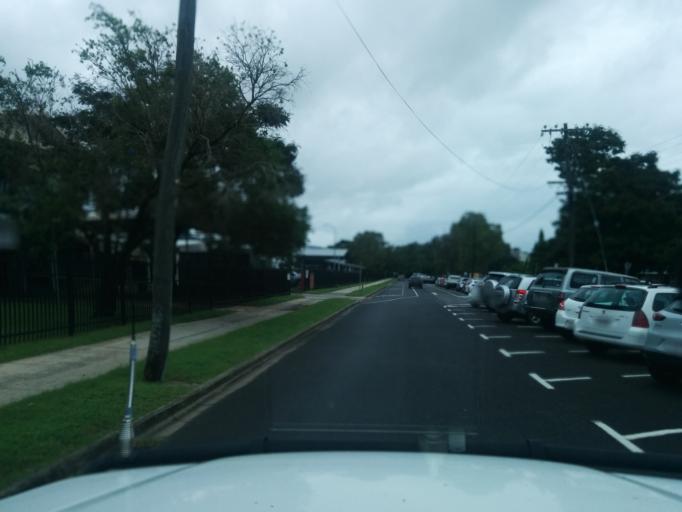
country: AU
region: Queensland
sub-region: Cairns
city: Cairns
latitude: -16.9226
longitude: 145.7536
